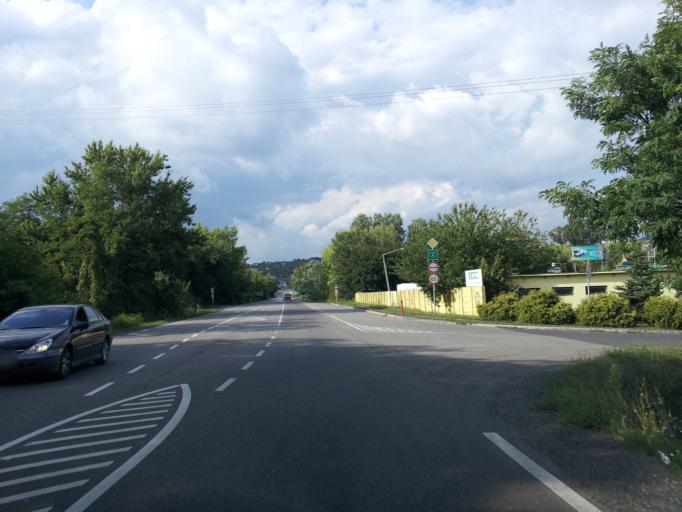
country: HU
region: Pest
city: Vac
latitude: 47.8104
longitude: 19.0941
